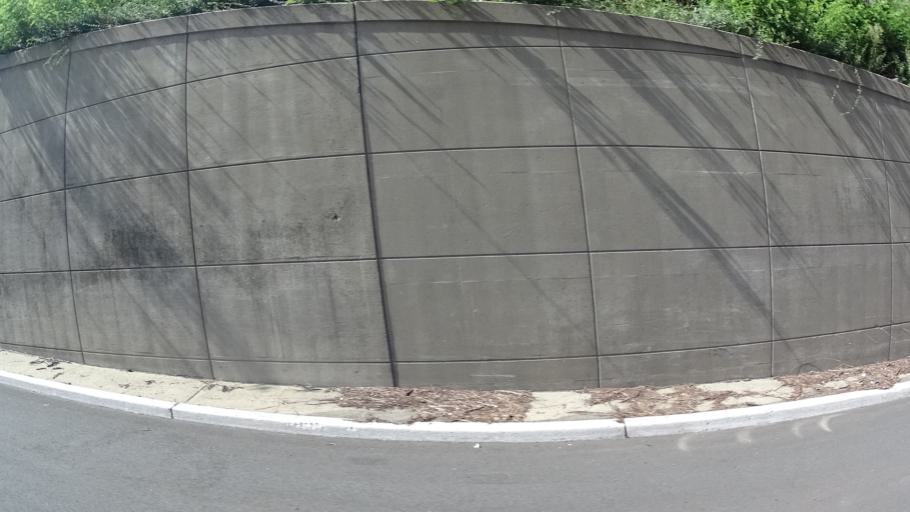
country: US
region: New Jersey
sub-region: Union County
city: Summit
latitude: 40.7338
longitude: -74.3551
